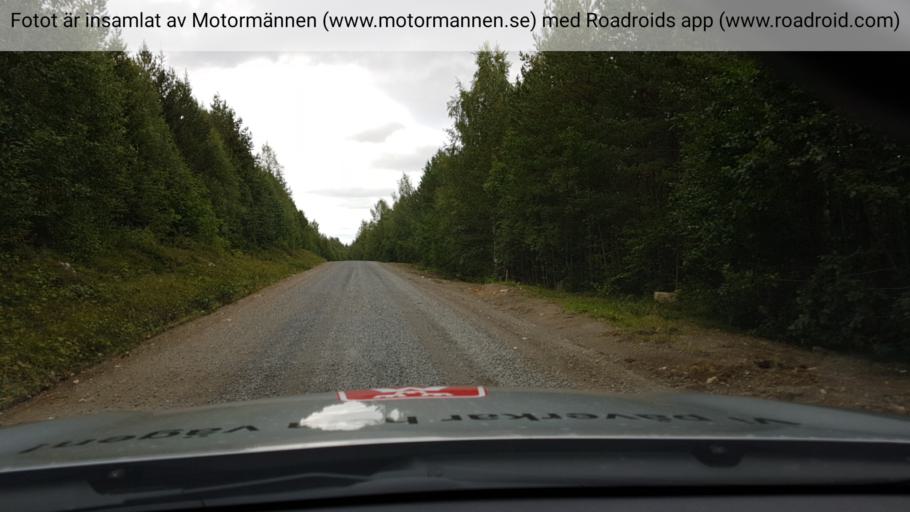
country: SE
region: Jaemtland
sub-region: Ragunda Kommun
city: Hammarstrand
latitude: 62.8919
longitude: 16.0613
